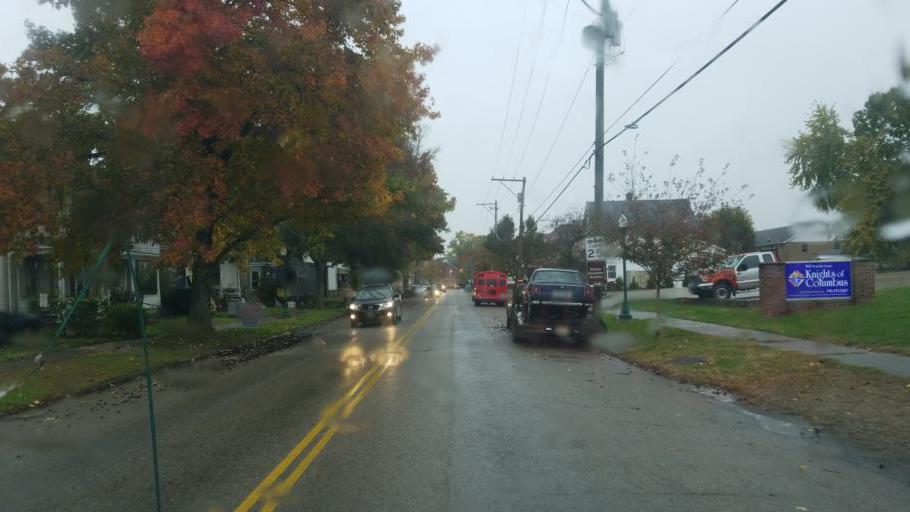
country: US
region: Ohio
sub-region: Washington County
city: Marietta
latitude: 39.4117
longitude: -81.4611
